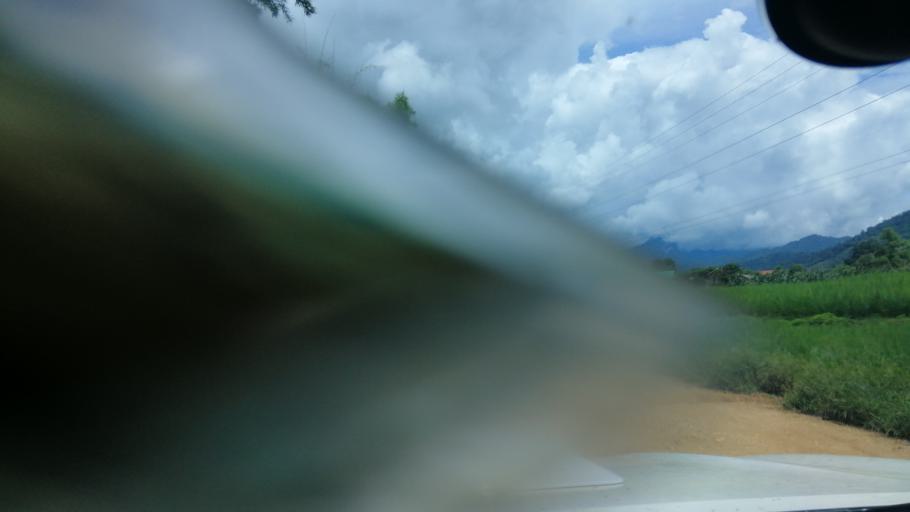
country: TH
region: Phayao
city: Phu Sang
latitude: 19.6819
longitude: 100.5026
